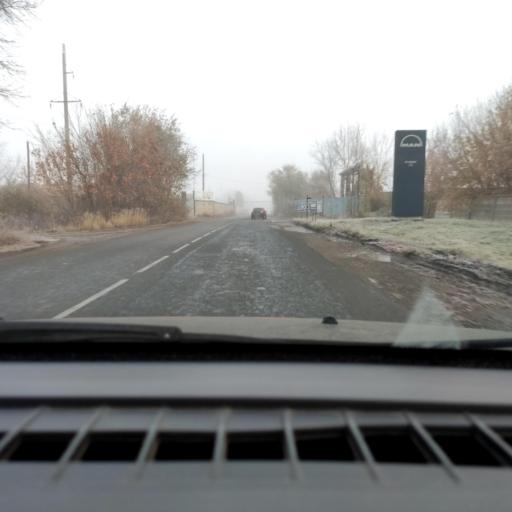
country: RU
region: Samara
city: Tol'yatti
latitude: 53.5845
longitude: 49.2570
